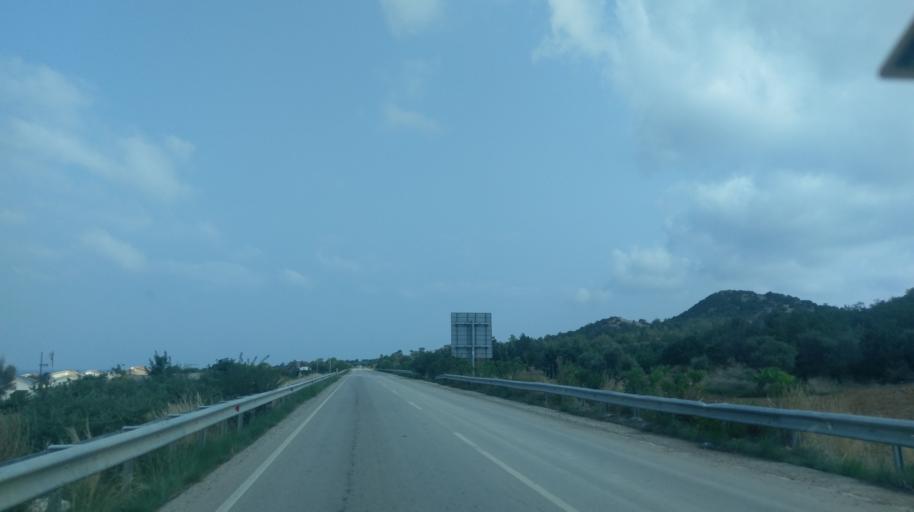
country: CY
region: Ammochostos
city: Lefkonoiko
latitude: 35.3737
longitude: 33.7129
